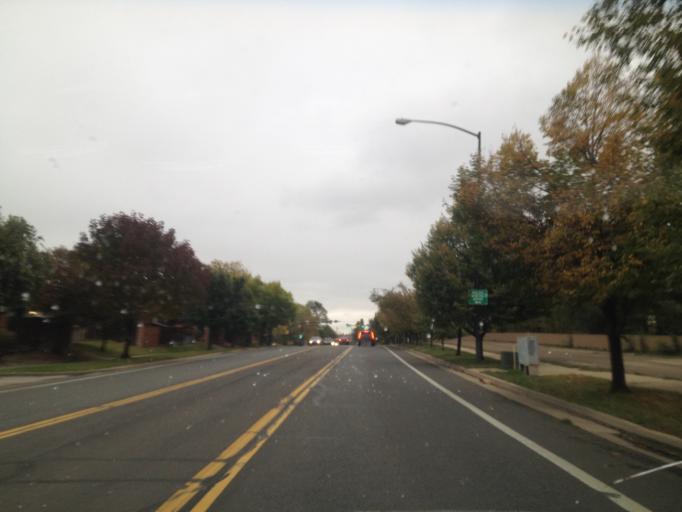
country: US
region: Colorado
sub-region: Boulder County
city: Boulder
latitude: 40.0292
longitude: -105.2368
